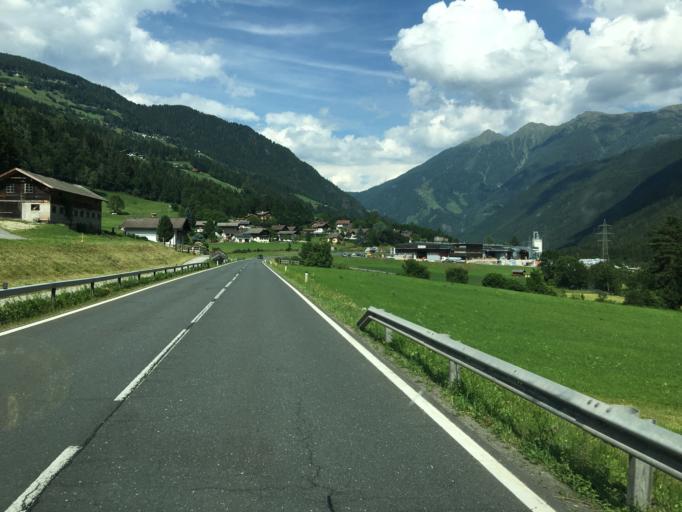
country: AT
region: Carinthia
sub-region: Politischer Bezirk Spittal an der Drau
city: Stall
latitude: 46.8805
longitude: 13.0133
